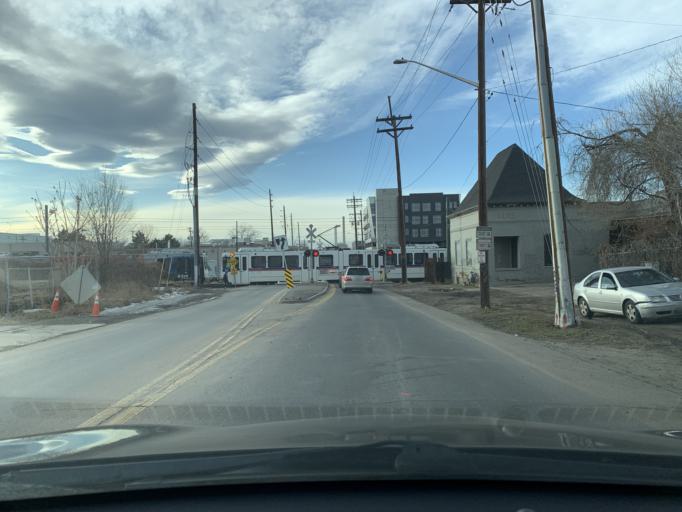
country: US
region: Colorado
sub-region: Denver County
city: Denver
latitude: 39.7369
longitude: -105.0056
